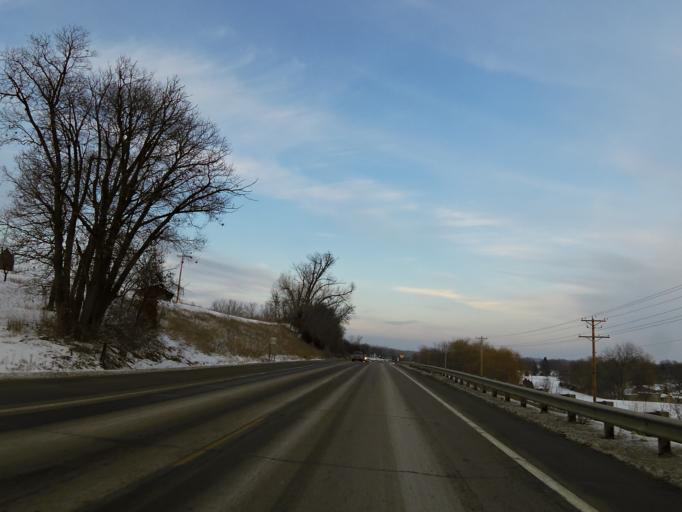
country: US
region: Minnesota
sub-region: Carver County
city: Chaska
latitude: 44.7833
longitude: -93.6111
